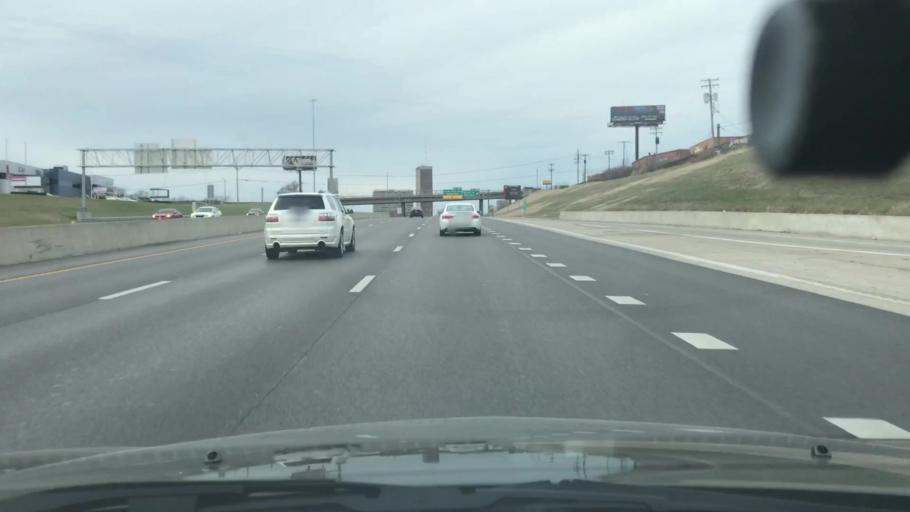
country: US
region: Missouri
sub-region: City of Saint Louis
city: St. Louis
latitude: 38.6281
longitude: -90.2192
